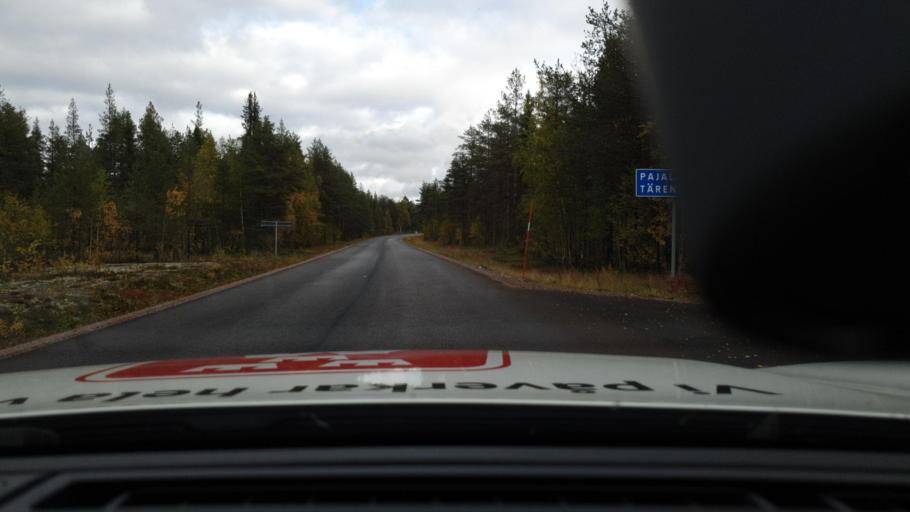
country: SE
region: Norrbotten
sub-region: Gallivare Kommun
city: Gaellivare
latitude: 67.0113
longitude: 21.8388
